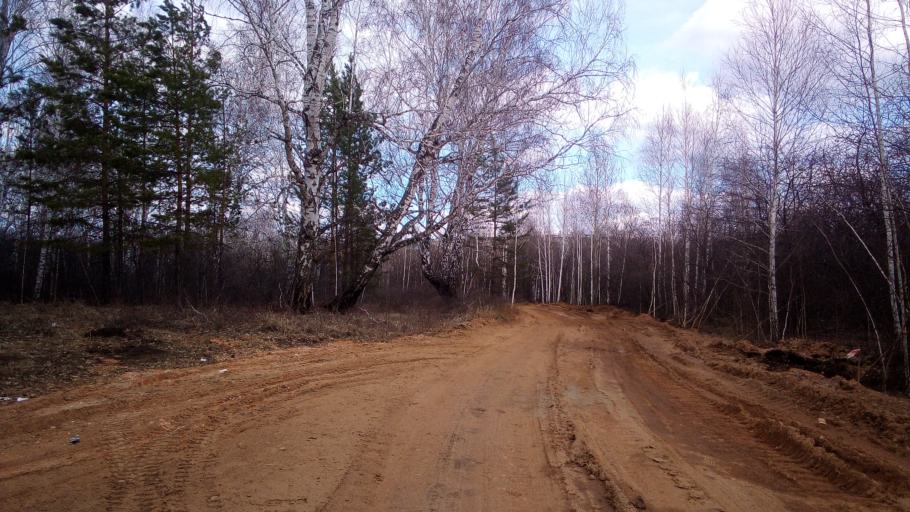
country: RU
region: Chelyabinsk
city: Sargazy
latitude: 55.1240
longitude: 61.2574
